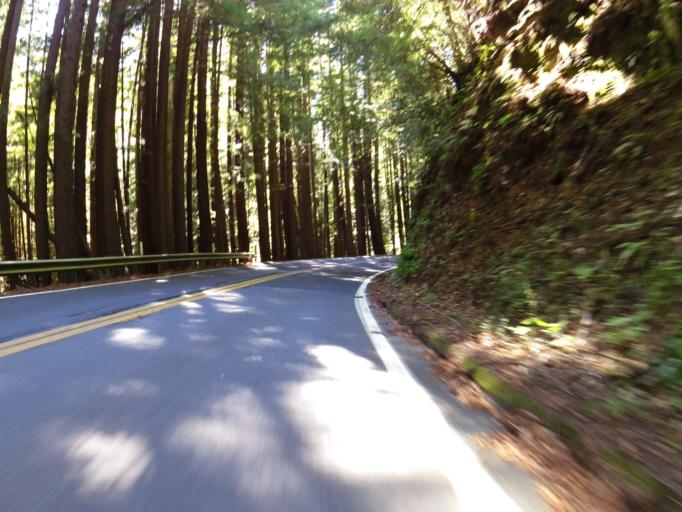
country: US
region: California
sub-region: Humboldt County
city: Redway
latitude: 39.7937
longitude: -123.8166
